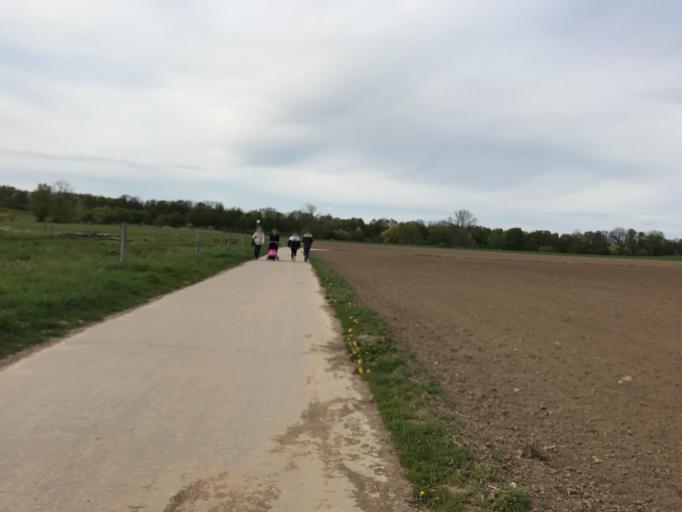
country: DE
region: Rheinland-Pfalz
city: Sorgenloch
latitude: 49.8938
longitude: 8.1933
